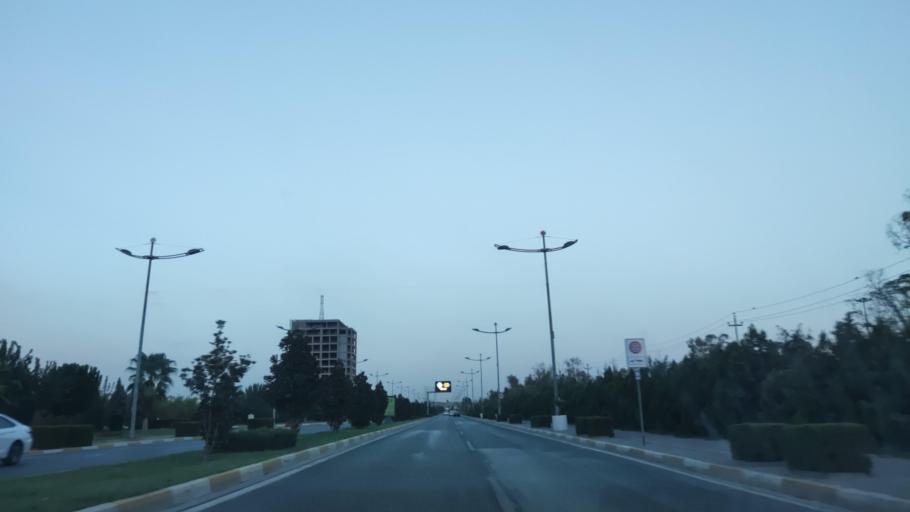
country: IQ
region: Arbil
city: Erbil
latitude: 36.1992
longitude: 43.9823
